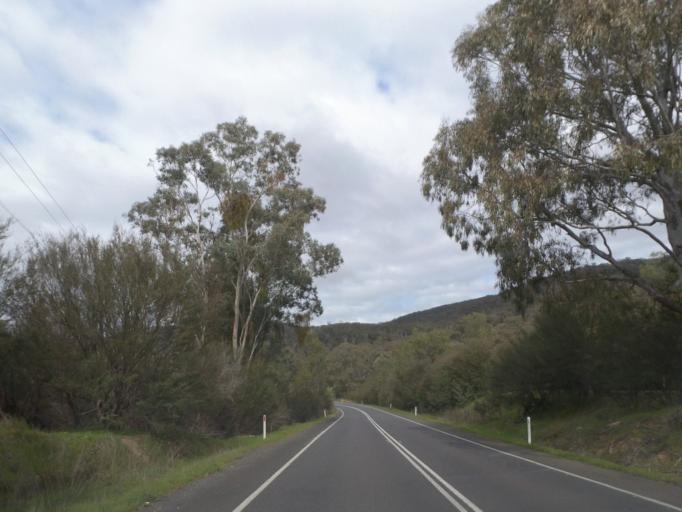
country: AU
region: Victoria
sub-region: Murrindindi
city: Kinglake West
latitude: -37.1347
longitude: 145.2314
